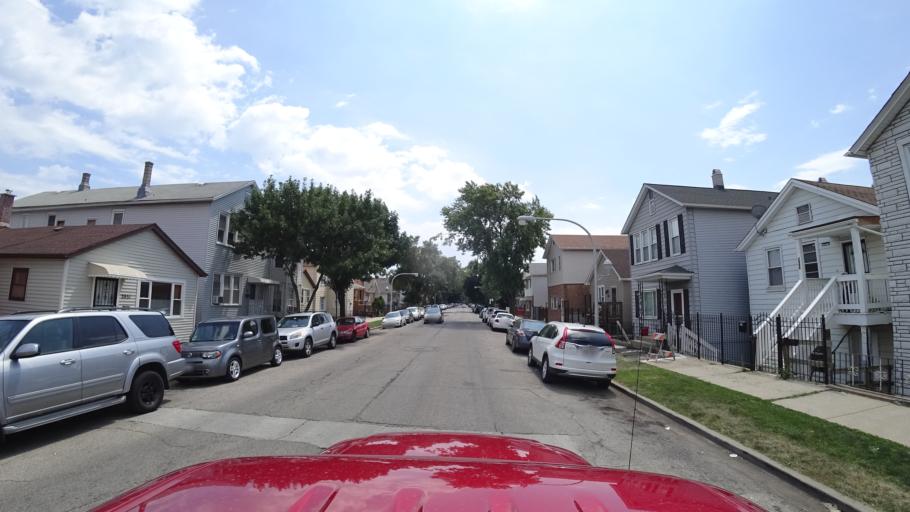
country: US
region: Illinois
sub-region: Cook County
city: Chicago
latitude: 41.8403
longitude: -87.6514
